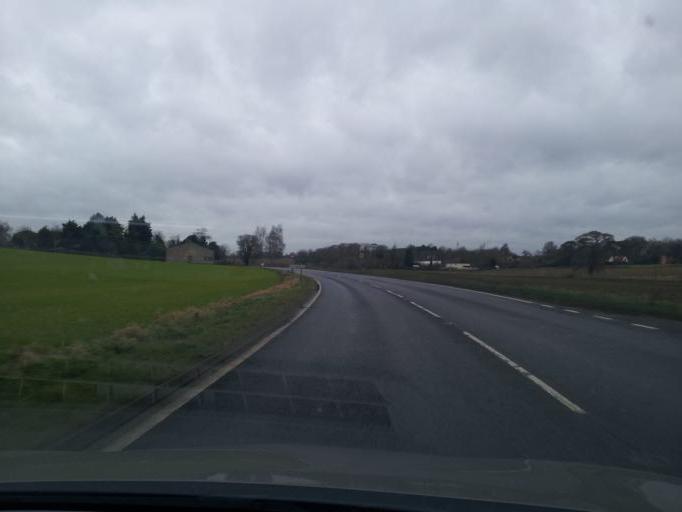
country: GB
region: England
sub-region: Suffolk
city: Botesdale
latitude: 52.3378
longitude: 0.9662
